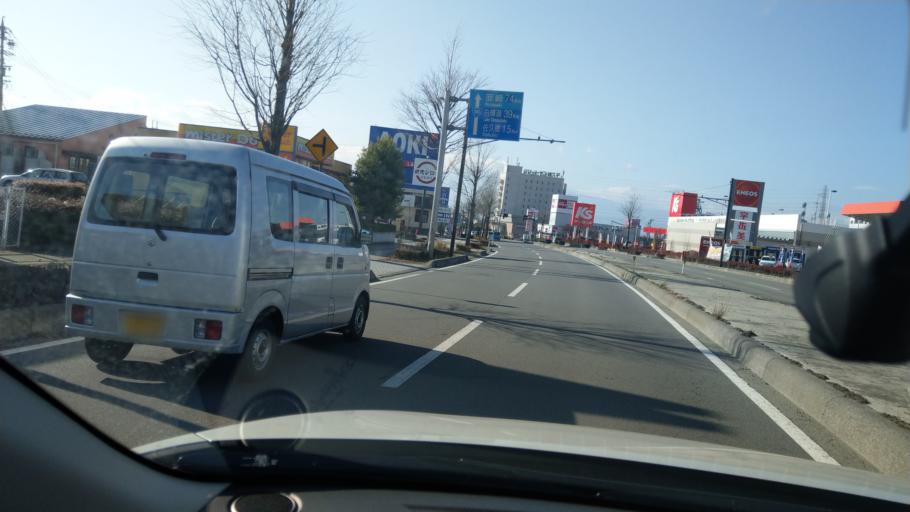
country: JP
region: Nagano
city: Komoro
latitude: 36.2798
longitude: 138.4692
